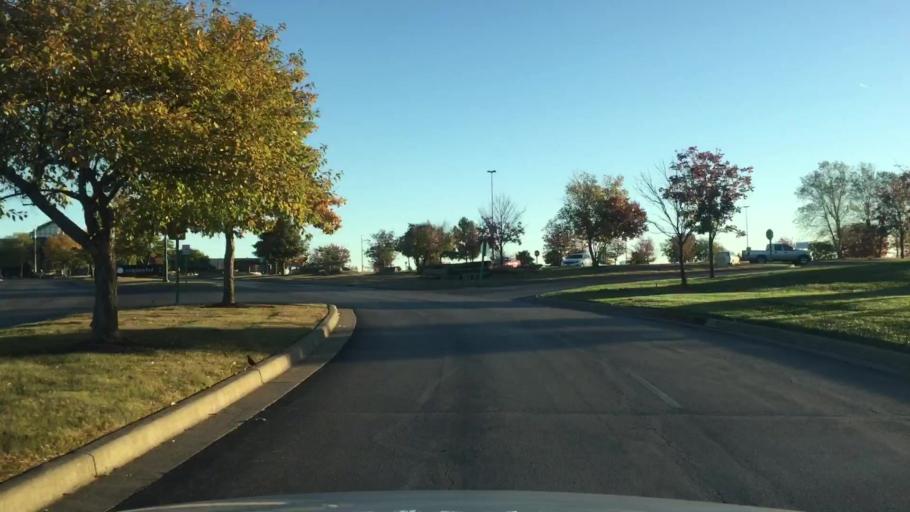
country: US
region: Kansas
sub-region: Wyandotte County
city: Edwardsville
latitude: 39.1188
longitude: -94.8170
